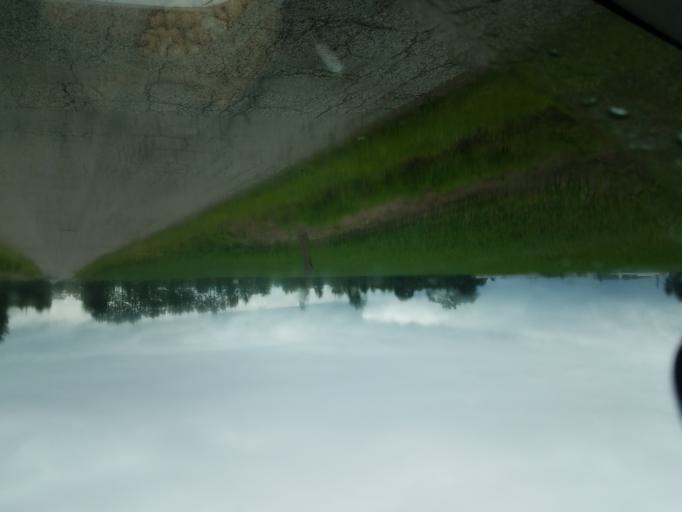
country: US
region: Ohio
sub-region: Morrow County
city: Cardington
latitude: 40.5281
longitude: -82.8986
